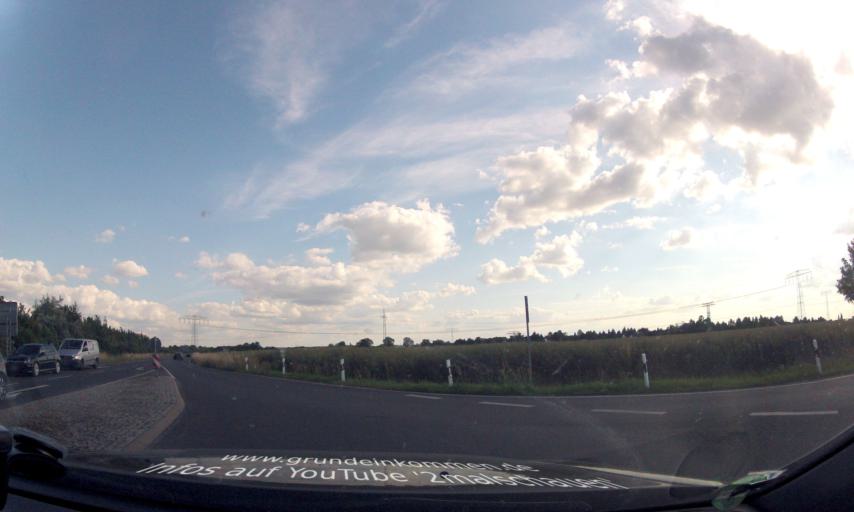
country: DE
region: Saxony
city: Borsdorf
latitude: 51.3551
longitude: 12.5212
